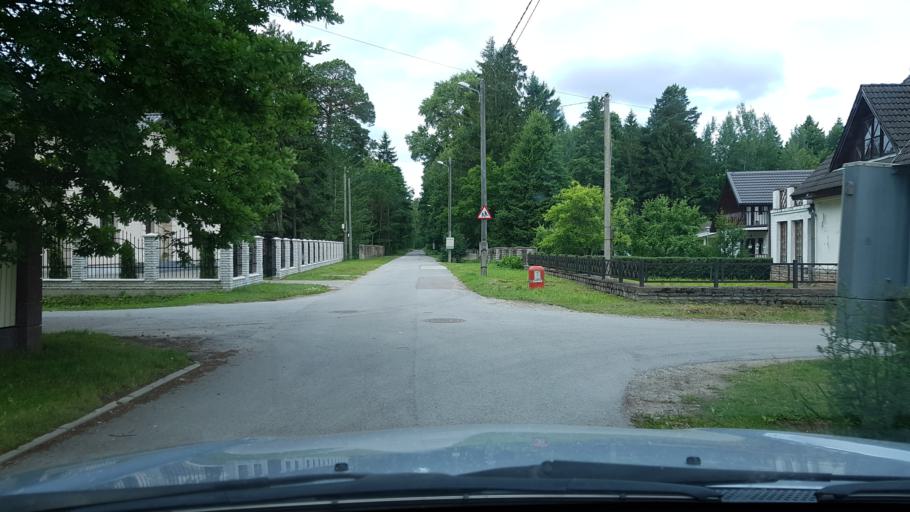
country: EE
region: Ida-Virumaa
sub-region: Narva-Joesuu linn
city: Narva-Joesuu
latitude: 59.4479
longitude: 28.0253
